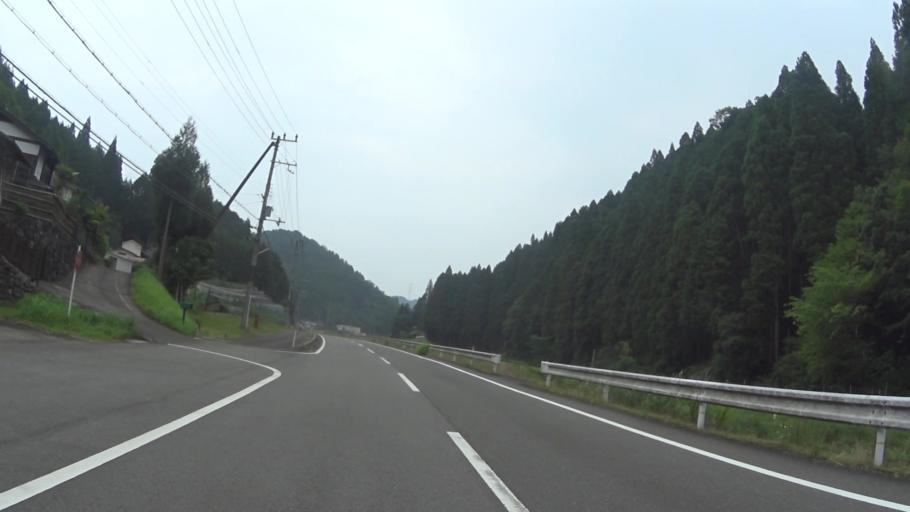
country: JP
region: Kyoto
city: Kameoka
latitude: 35.1573
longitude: 135.5983
